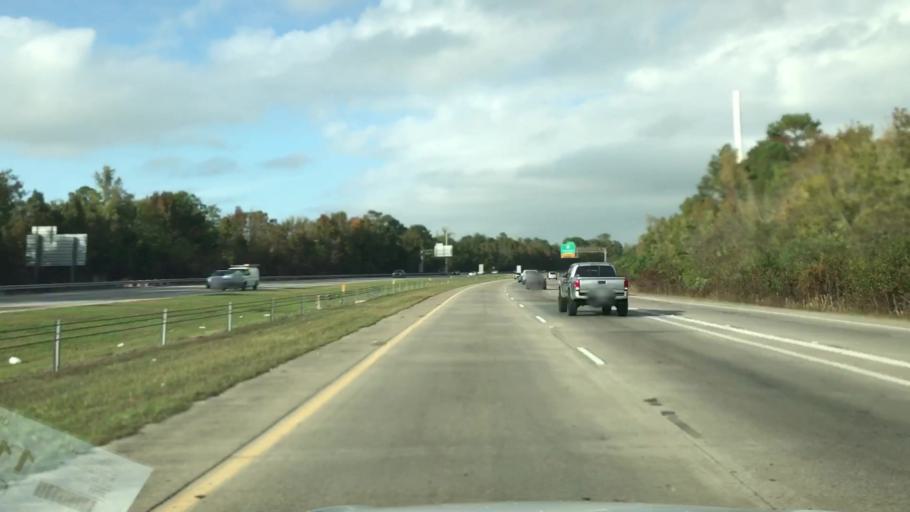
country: US
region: South Carolina
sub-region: Berkeley County
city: Hanahan
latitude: 32.8735
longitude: -80.0267
